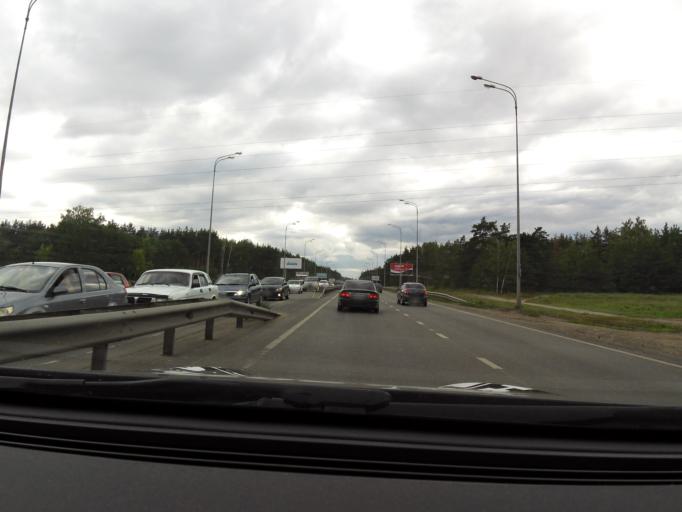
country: RU
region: Tatarstan
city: Staroye Arakchino
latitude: 55.8284
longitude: 49.0124
